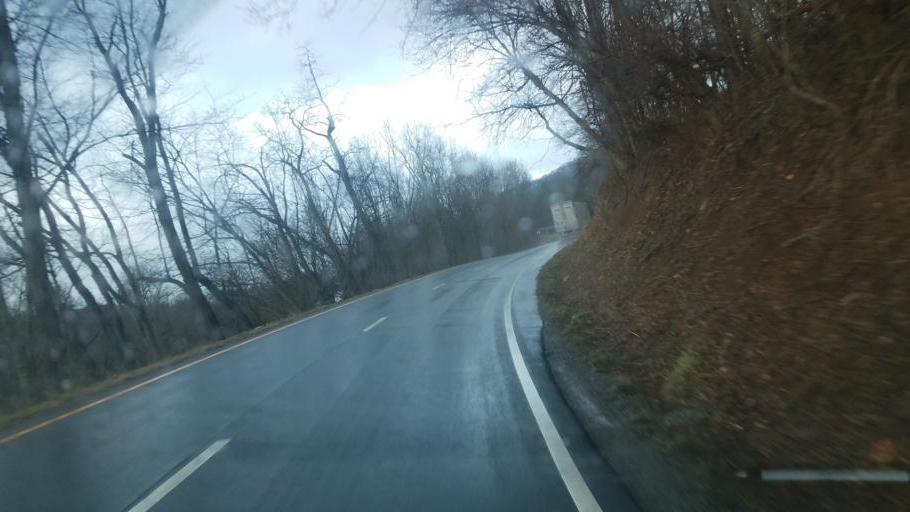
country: US
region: Virginia
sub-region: Giles County
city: Pearisburg
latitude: 37.3041
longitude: -80.7380
